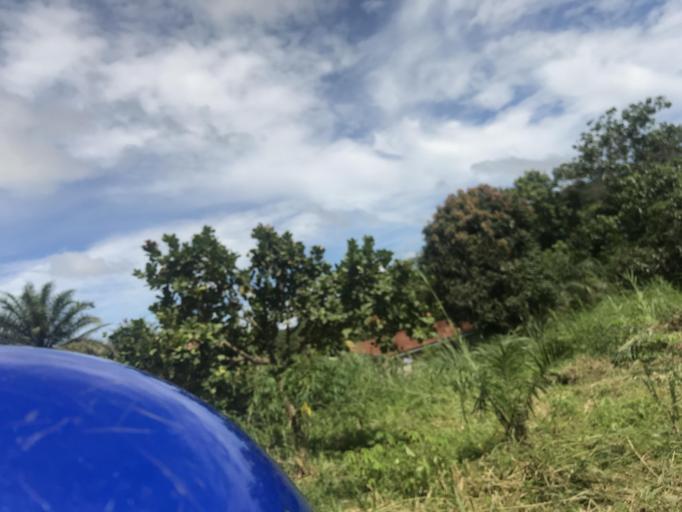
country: SL
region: Eastern Province
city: Koidu
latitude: 8.6473
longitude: -10.9871
